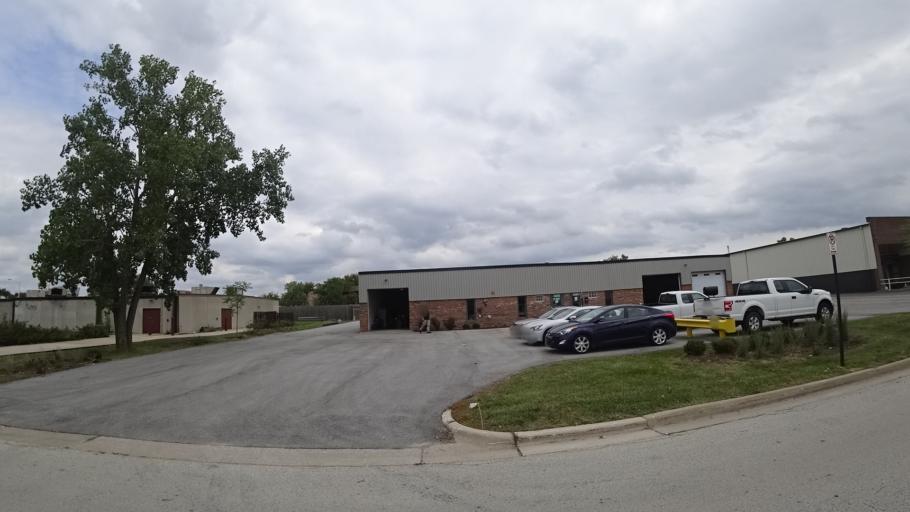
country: US
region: Illinois
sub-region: Cook County
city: Tinley Park
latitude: 41.5723
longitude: -87.8016
